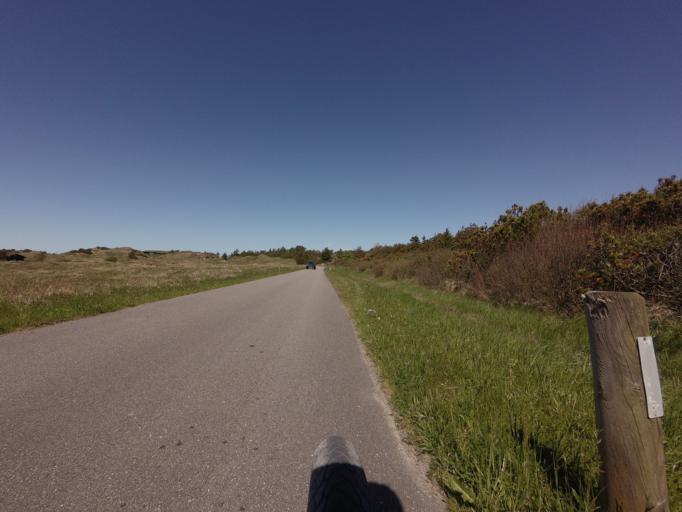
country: DK
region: North Denmark
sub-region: Jammerbugt Kommune
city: Pandrup
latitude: 57.2276
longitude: 9.5660
